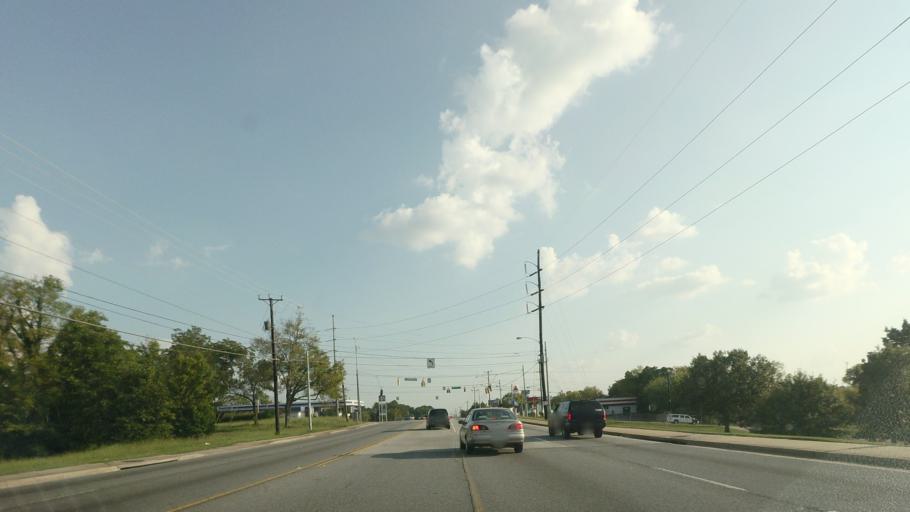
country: US
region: Georgia
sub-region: Bibb County
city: Macon
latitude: 32.8267
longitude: -83.6628
